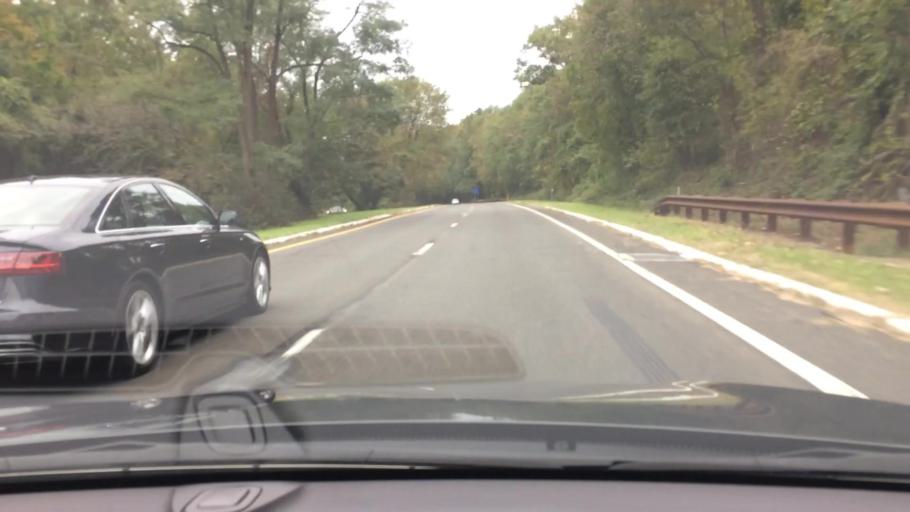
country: US
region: New York
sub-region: Rockland County
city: Sparkill
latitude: 41.0137
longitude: -73.9247
